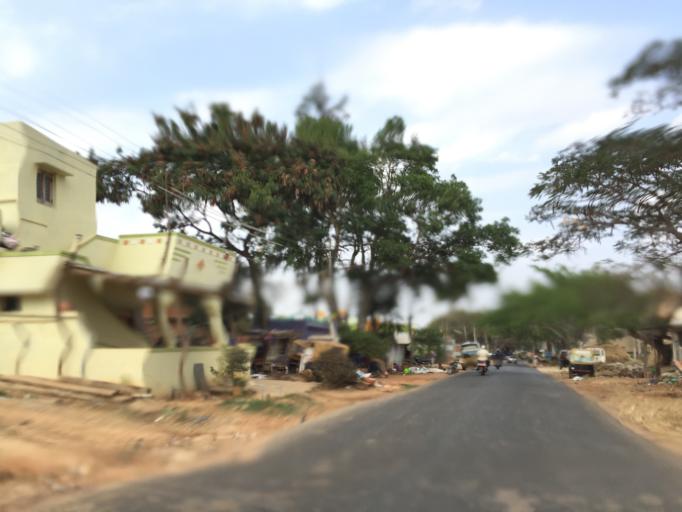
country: IN
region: Karnataka
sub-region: Chikkaballapur
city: Chik Ballapur
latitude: 13.4142
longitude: 77.7177
